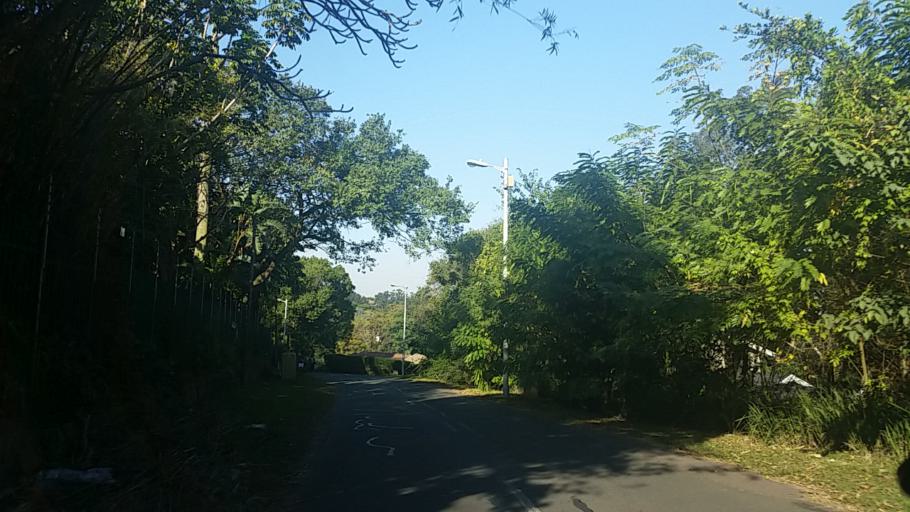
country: ZA
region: KwaZulu-Natal
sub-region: eThekwini Metropolitan Municipality
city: Berea
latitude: -29.8404
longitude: 30.9166
